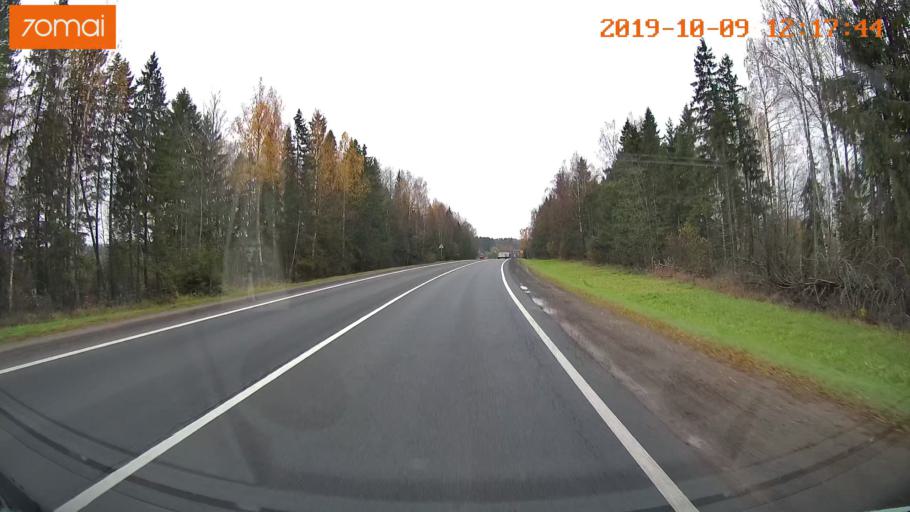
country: RU
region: Jaroslavl
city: Prechistoye
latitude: 58.4522
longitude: 40.3217
